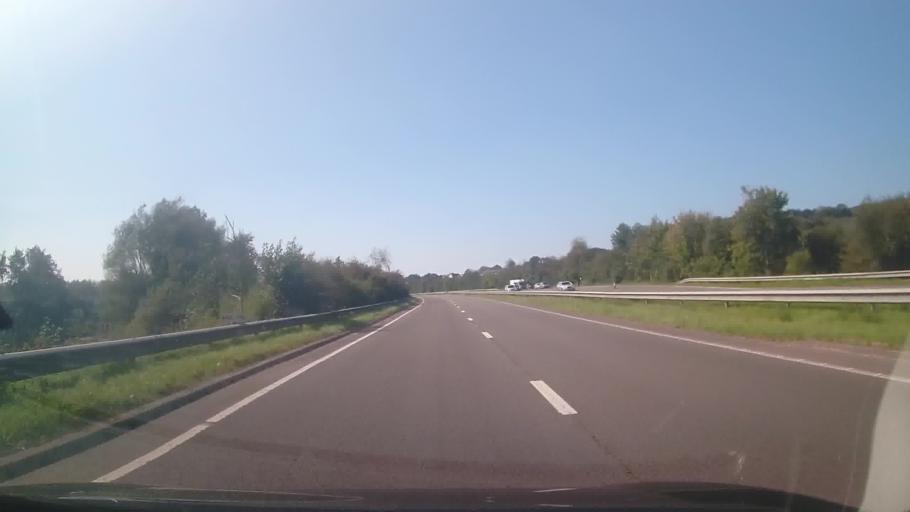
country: GB
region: Wales
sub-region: Carmarthenshire
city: Carmarthen
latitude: 51.8641
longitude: -4.2877
